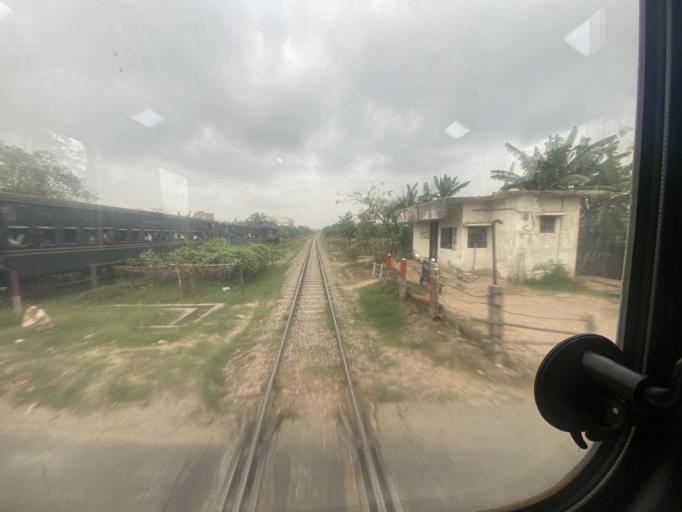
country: BD
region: Dhaka
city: Tungi
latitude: 23.9137
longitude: 90.4223
